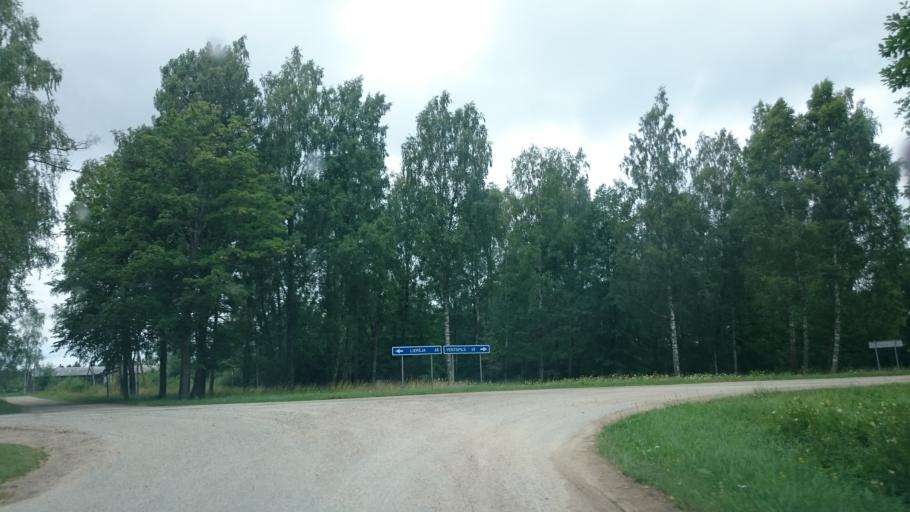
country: LV
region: Pavilostas
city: Pavilosta
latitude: 56.8621
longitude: 21.2227
